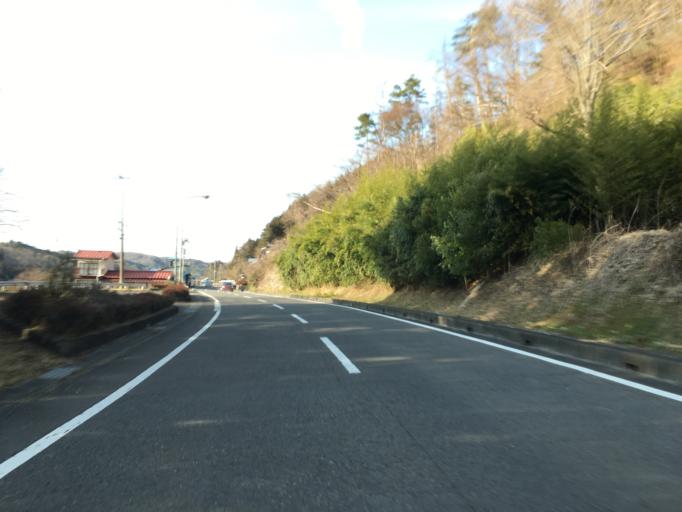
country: JP
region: Ibaraki
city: Daigo
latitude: 36.7562
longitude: 140.4385
